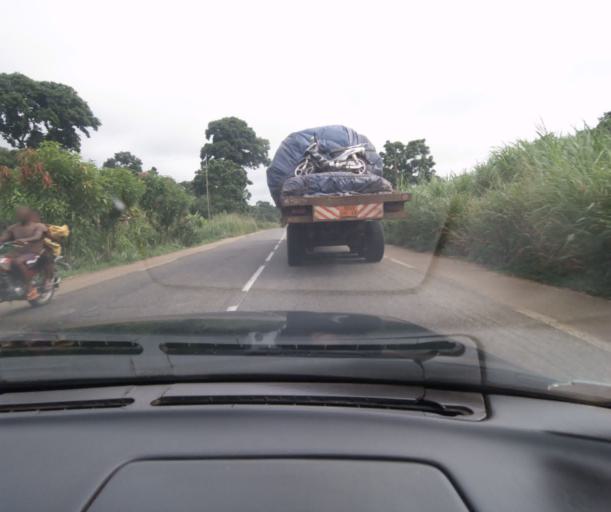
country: CM
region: Centre
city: Ombesa
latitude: 4.5908
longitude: 11.2629
